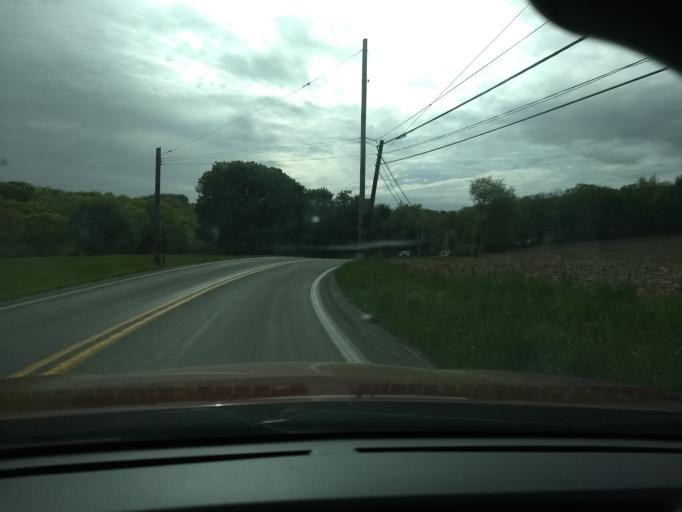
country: US
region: Pennsylvania
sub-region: Allegheny County
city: Bakerstown
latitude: 40.6016
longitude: -79.8987
